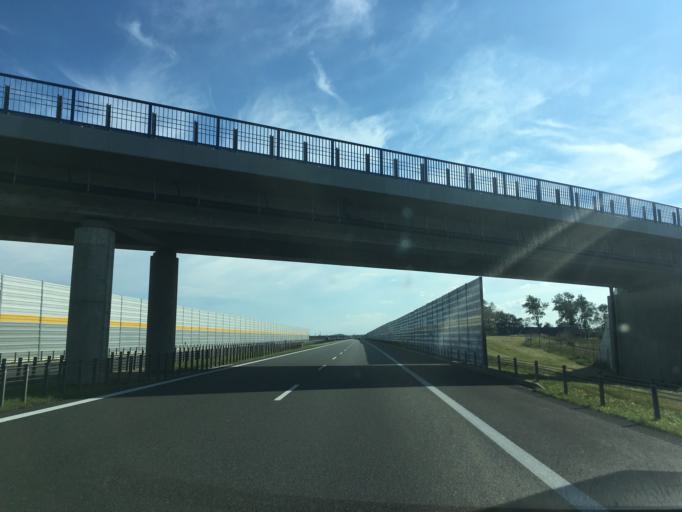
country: PL
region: Kujawsko-Pomorskie
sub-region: Powiat chelminski
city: Lisewo
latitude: 53.3081
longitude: 18.7061
